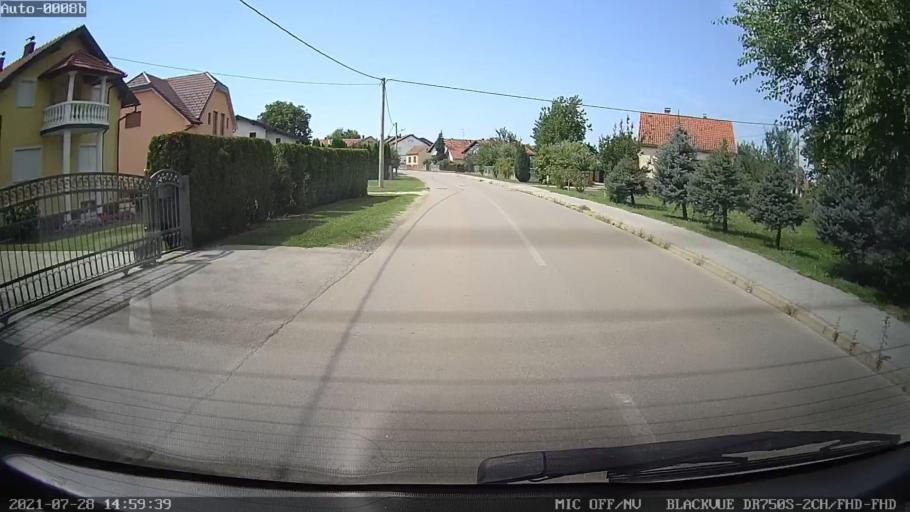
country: HR
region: Medimurska
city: Kursanec
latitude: 46.2843
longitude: 16.3869
